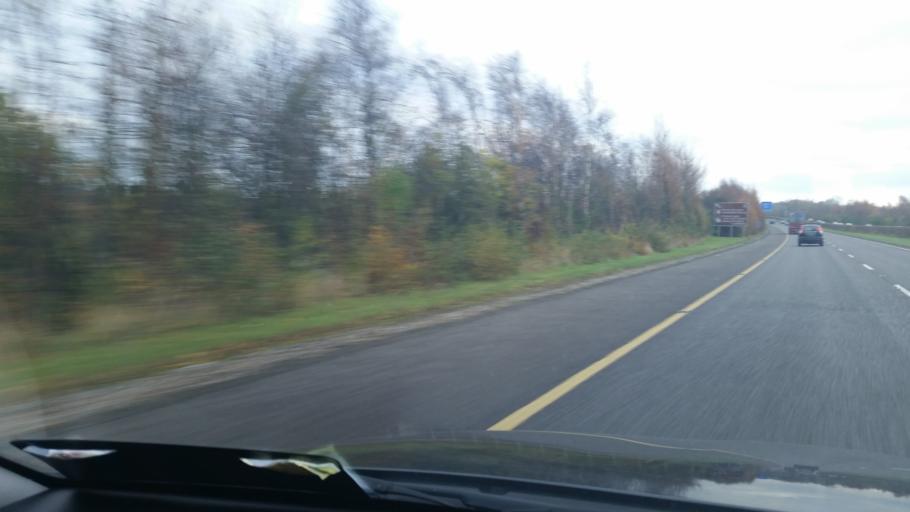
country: IE
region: Leinster
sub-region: An Mhi
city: Stamullin
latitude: 53.6147
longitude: -6.2416
